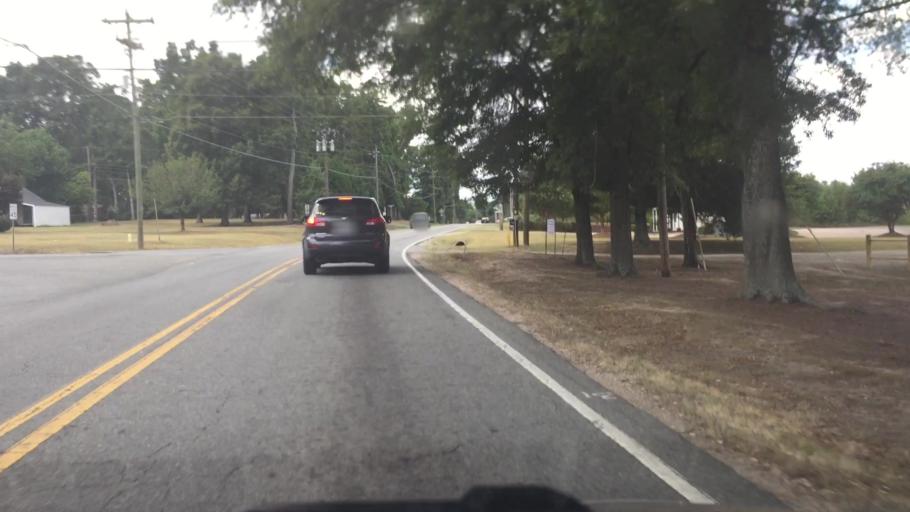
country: US
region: North Carolina
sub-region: Rowan County
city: Enochville
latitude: 35.5168
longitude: -80.6702
